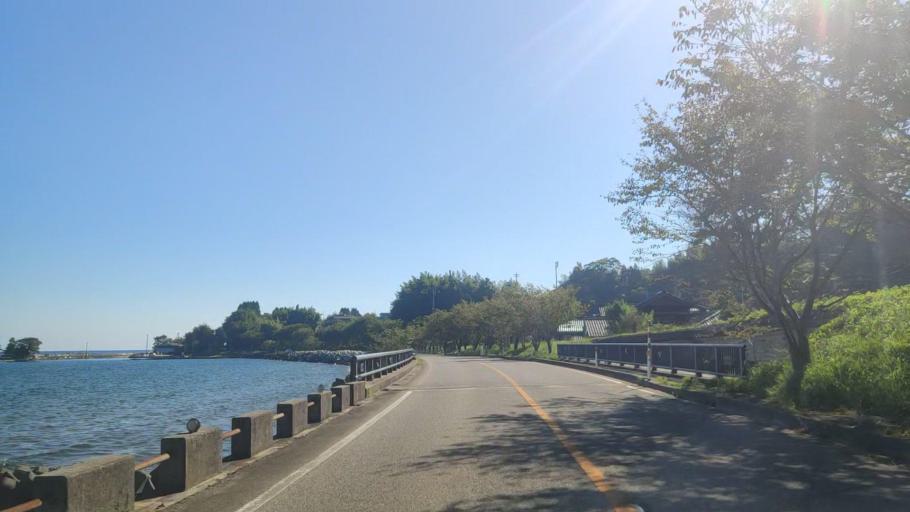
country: JP
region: Ishikawa
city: Nanao
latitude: 37.2776
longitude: 137.0974
